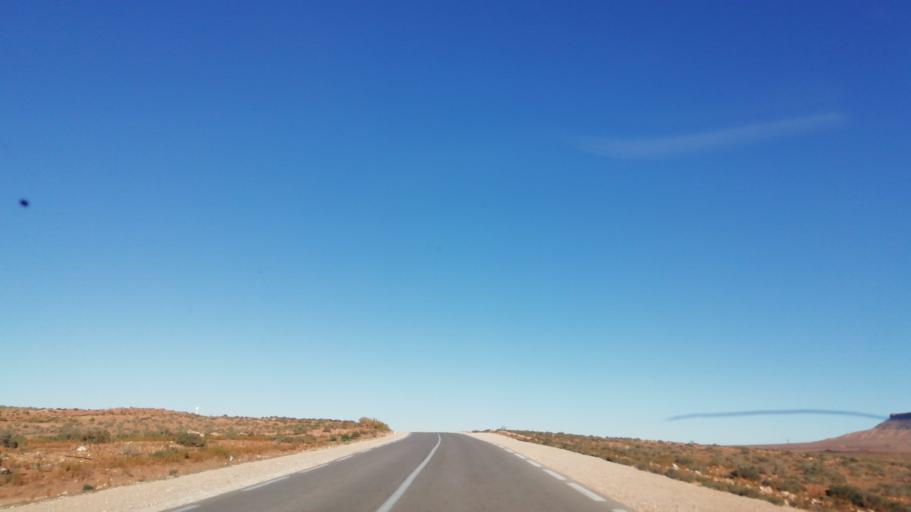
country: DZ
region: El Bayadh
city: El Abiodh Sidi Cheikh
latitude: 33.0943
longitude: 0.2001
